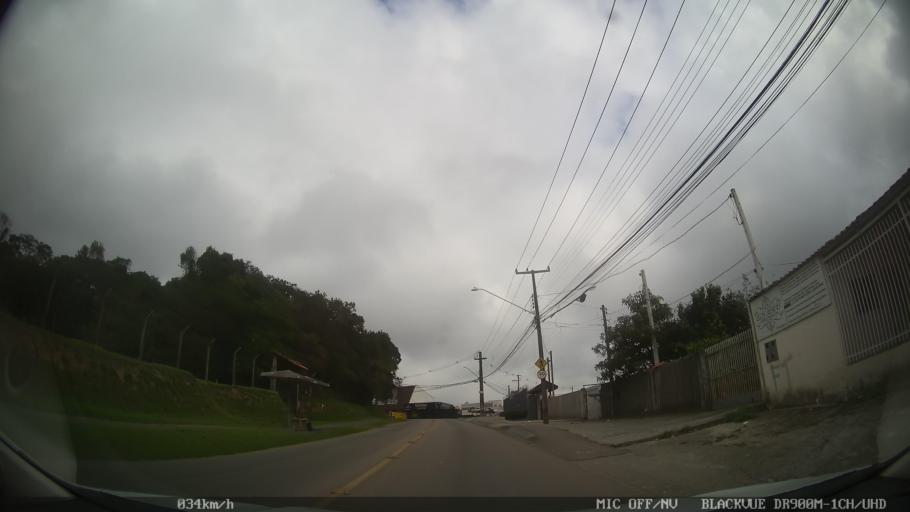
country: BR
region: Parana
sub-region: Almirante Tamandare
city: Almirante Tamandare
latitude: -25.3551
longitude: -49.2722
